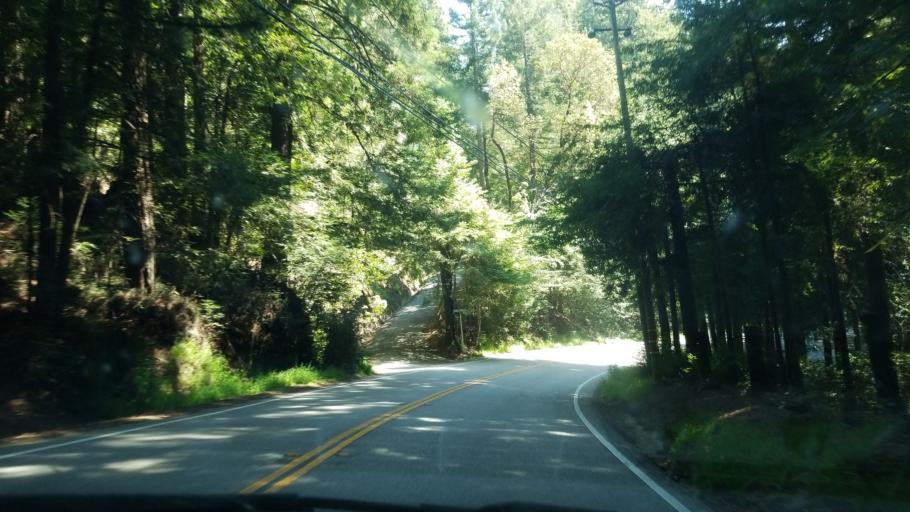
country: US
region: California
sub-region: Santa Clara County
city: Lexington Hills
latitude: 37.1072
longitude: -121.9452
